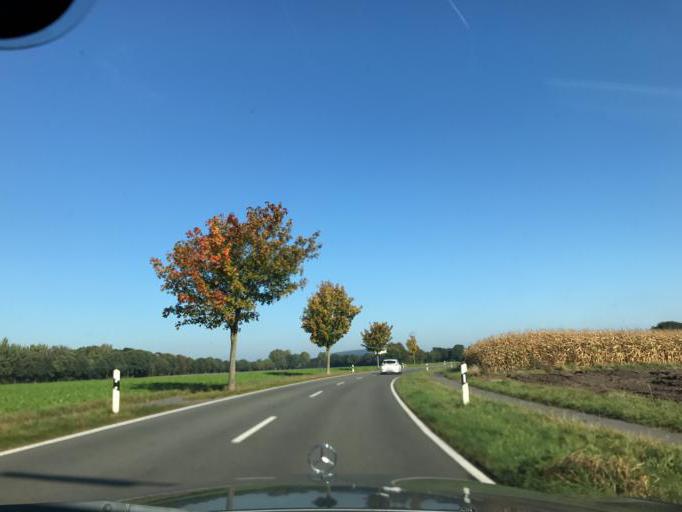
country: DE
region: Lower Saxony
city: Papenburg
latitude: 53.0744
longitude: 7.3457
